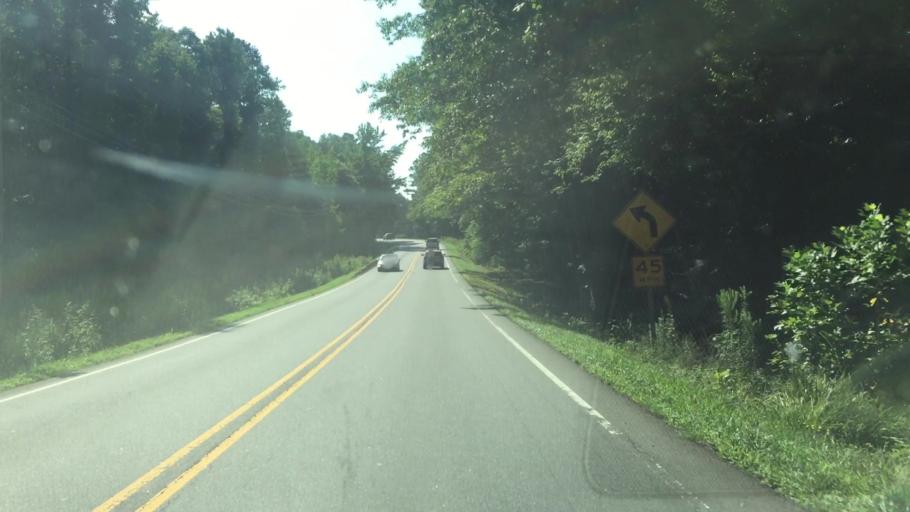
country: US
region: North Carolina
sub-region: Union County
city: Fairview
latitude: 35.1638
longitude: -80.5867
